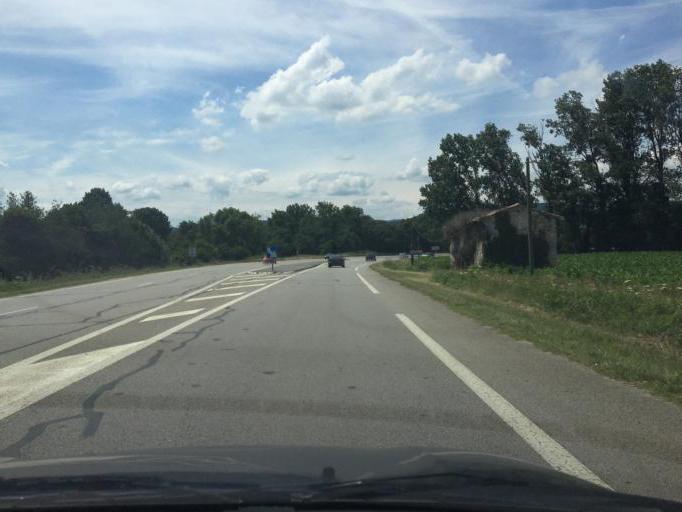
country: FR
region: Rhone-Alpes
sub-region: Departement de l'Ardeche
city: Charmes-sur-Rhone
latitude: 44.8458
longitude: 4.8550
